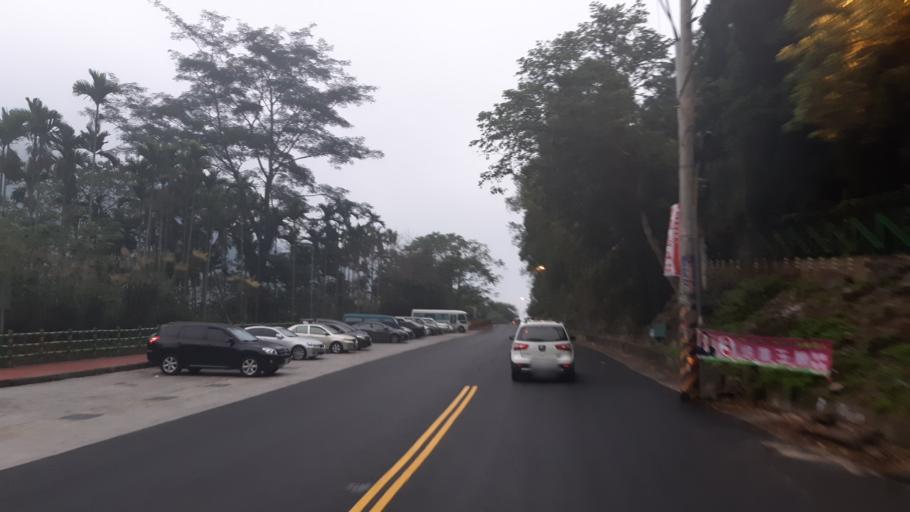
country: TW
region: Taiwan
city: Daxi
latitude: 24.7017
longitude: 121.1869
